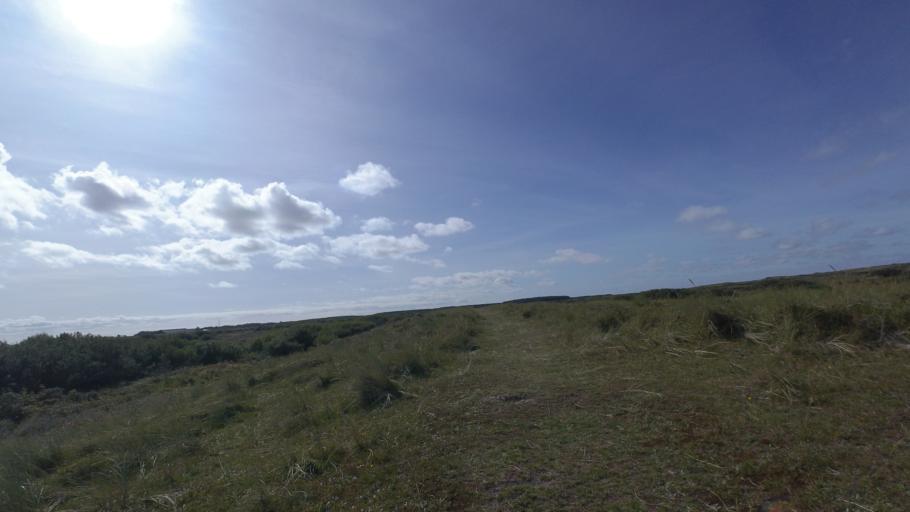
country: NL
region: Friesland
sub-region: Gemeente Ameland
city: Nes
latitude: 53.4548
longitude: 5.7368
